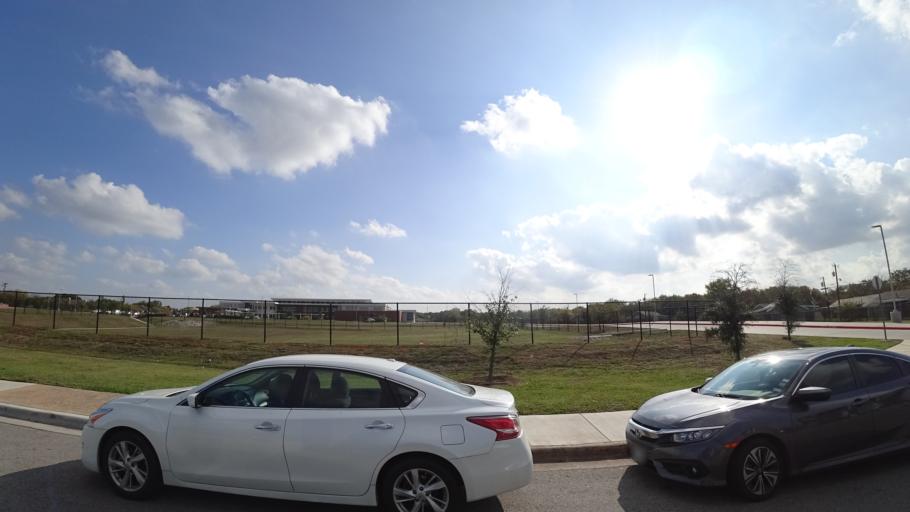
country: US
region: Texas
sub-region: Williamson County
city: Round Rock
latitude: 30.4980
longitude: -97.6728
